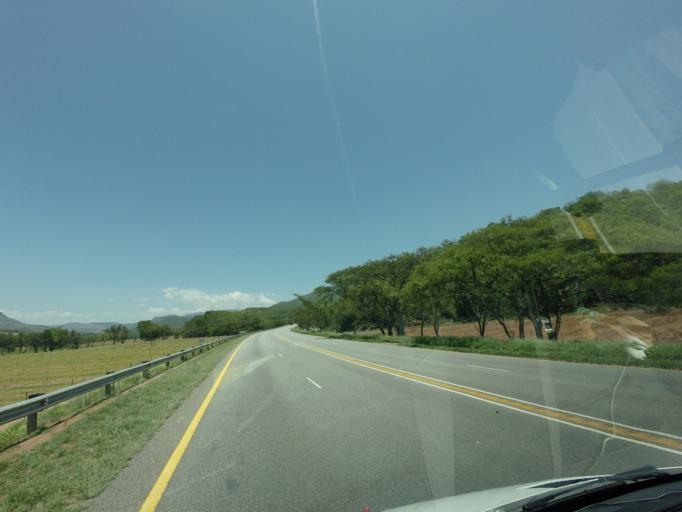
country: ZA
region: Mpumalanga
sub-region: Ehlanzeni District
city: Nelspruit
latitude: -25.4303
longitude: 30.7517
